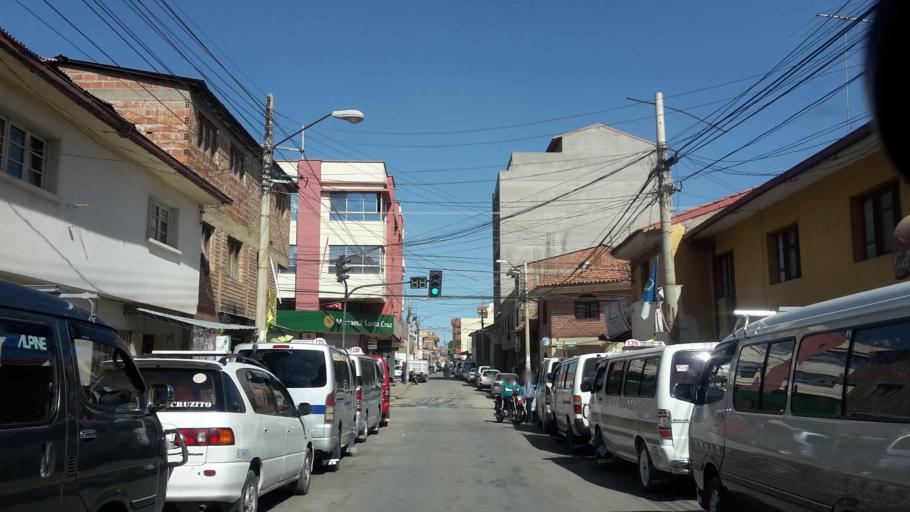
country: BO
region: Cochabamba
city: Cochabamba
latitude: -17.3384
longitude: -66.2217
